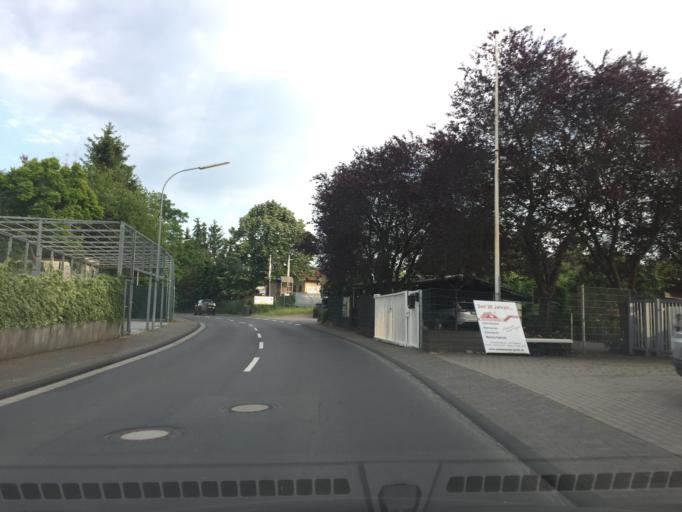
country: DE
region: Rheinland-Pfalz
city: Sankt Sebastian
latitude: 50.4267
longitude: 7.5653
